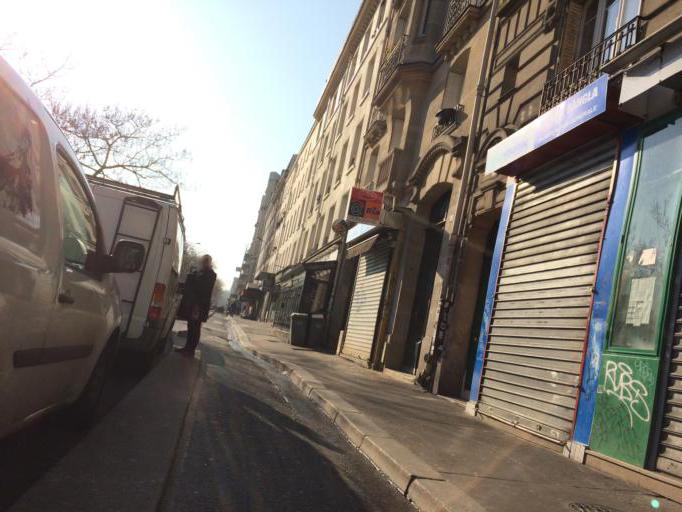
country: FR
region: Ile-de-France
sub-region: Departement de Seine-Saint-Denis
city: Le Pre-Saint-Gervais
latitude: 48.8665
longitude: 2.3831
